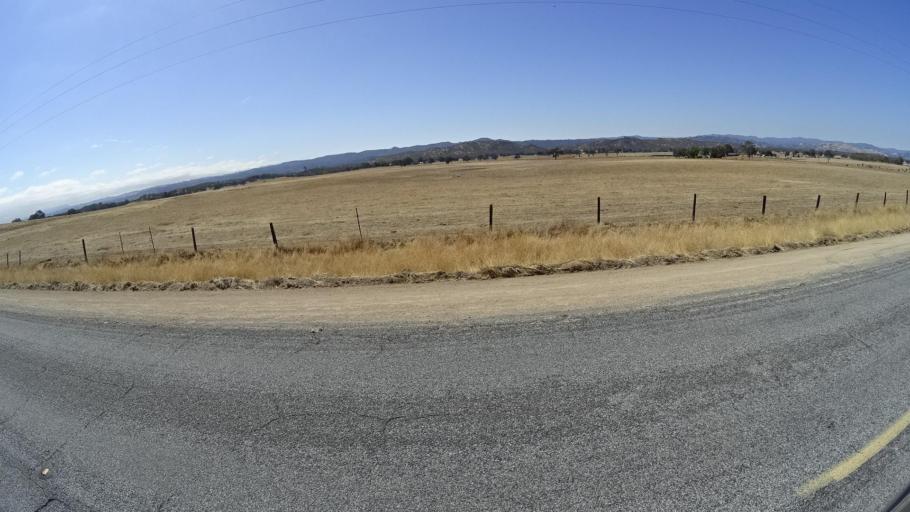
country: US
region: California
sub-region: San Luis Obispo County
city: Lake Nacimiento
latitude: 35.9345
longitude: -121.0593
